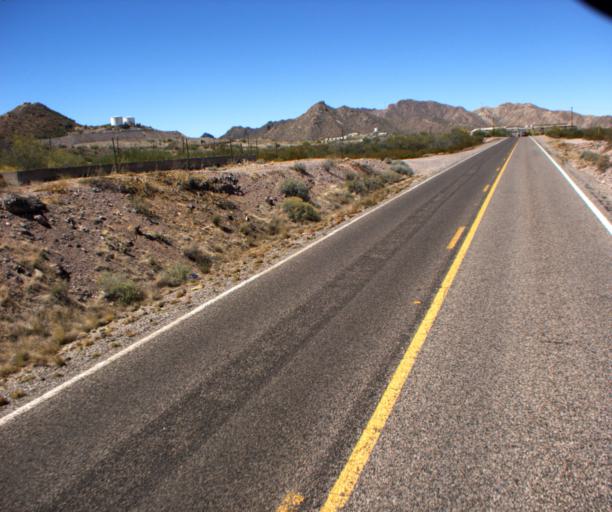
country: US
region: Arizona
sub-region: Pima County
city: Ajo
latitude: 32.3686
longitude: -112.8475
